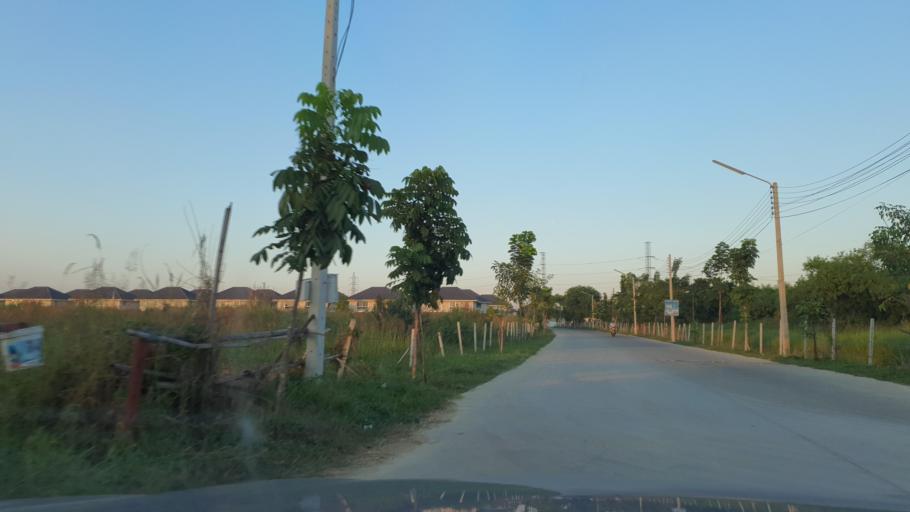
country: TH
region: Chiang Mai
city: Saraphi
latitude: 18.7249
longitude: 99.0757
